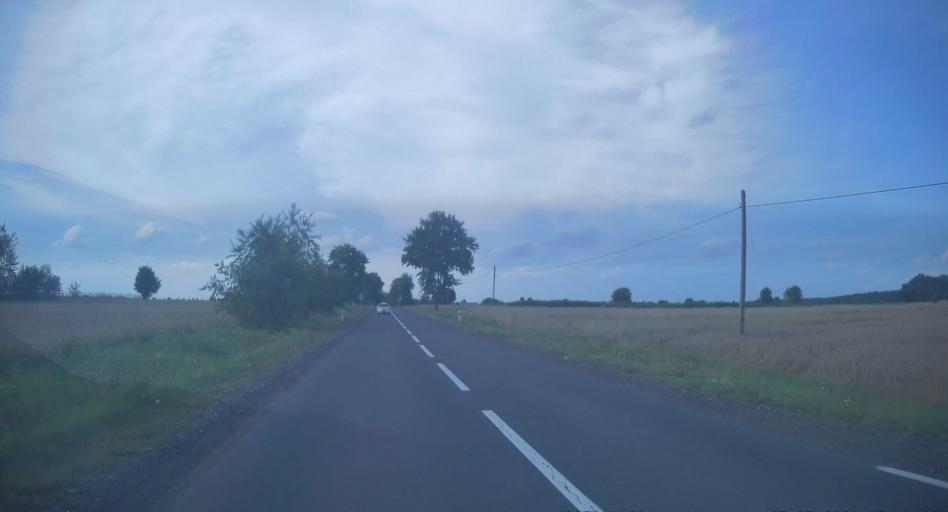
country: PL
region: Lodz Voivodeship
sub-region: Powiat rawski
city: Rawa Mazowiecka
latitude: 51.6873
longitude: 20.2673
